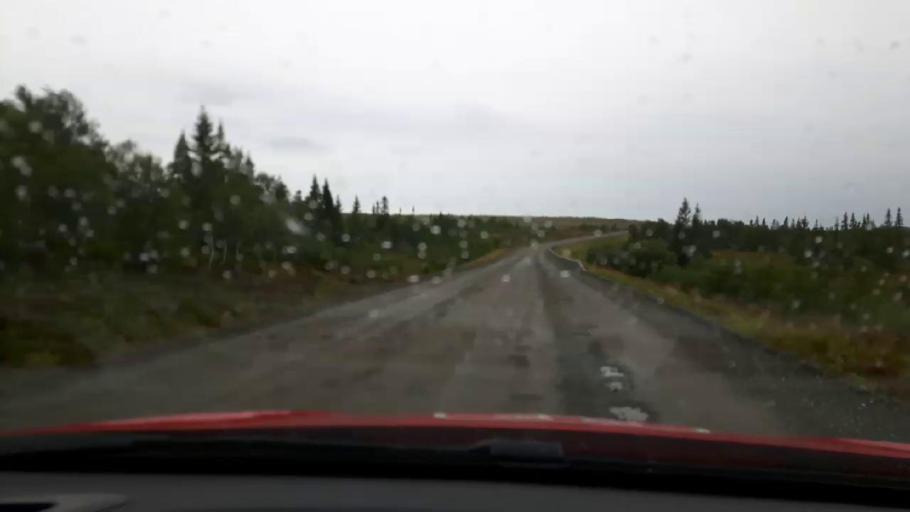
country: NO
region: Nord-Trondelag
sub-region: Meraker
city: Meraker
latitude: 63.6287
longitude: 12.2864
